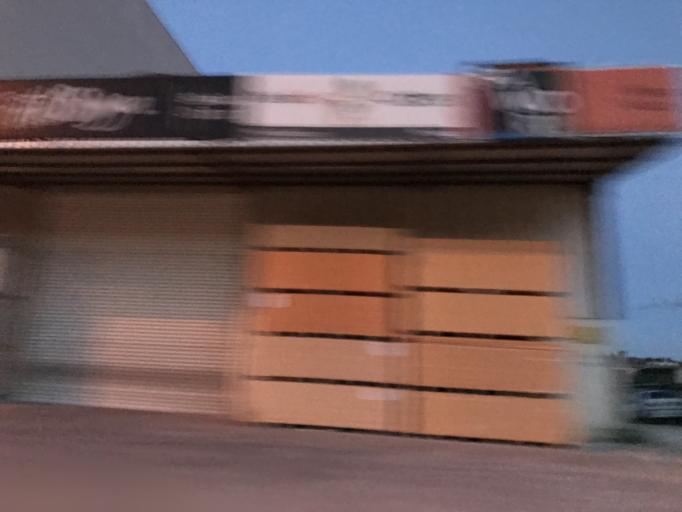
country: TR
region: Hatay
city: Asagiokcular
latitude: 36.1847
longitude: 36.1210
